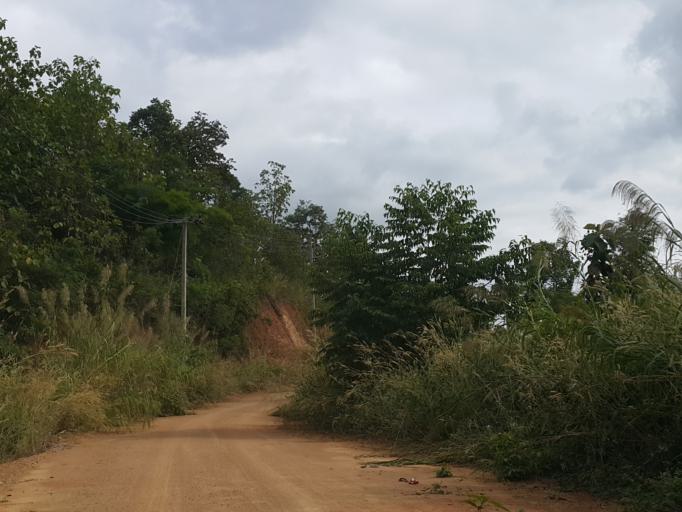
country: TH
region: Lampang
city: Chae Hom
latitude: 18.5761
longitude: 99.4423
